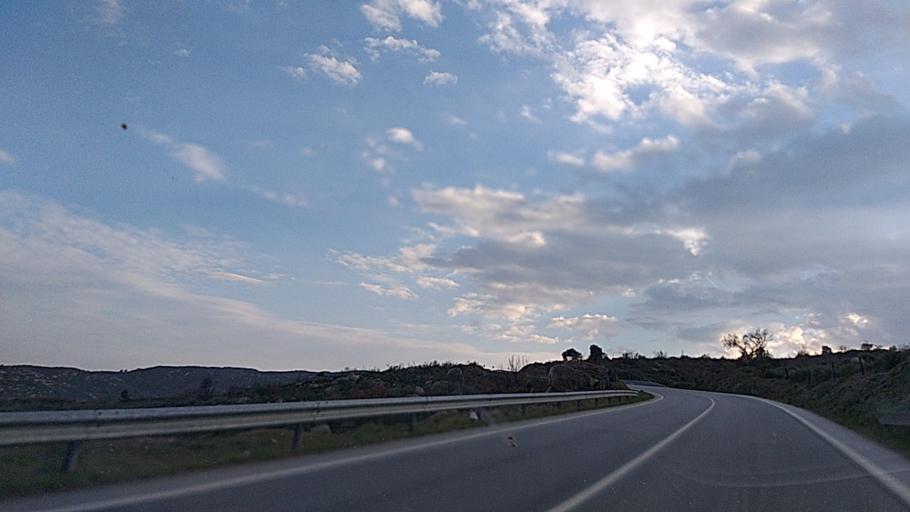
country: ES
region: Castille and Leon
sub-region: Provincia de Salamanca
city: Aldea del Obispo
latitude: 40.6971
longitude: -6.9343
